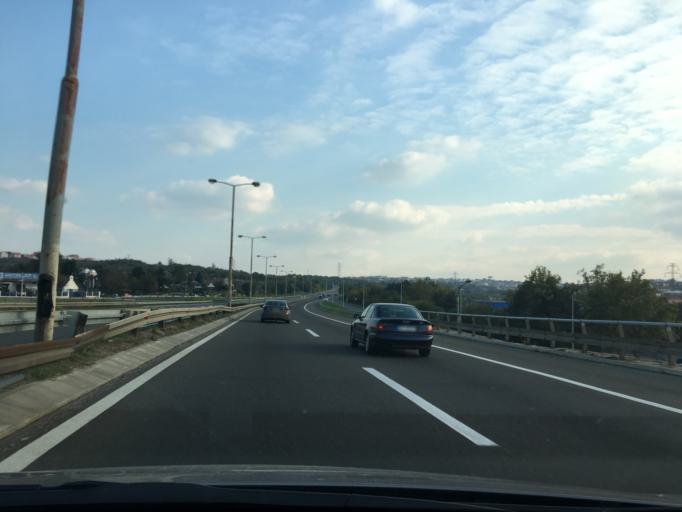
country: RS
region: Central Serbia
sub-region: Belgrade
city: Zvezdara
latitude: 44.7730
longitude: 20.5188
